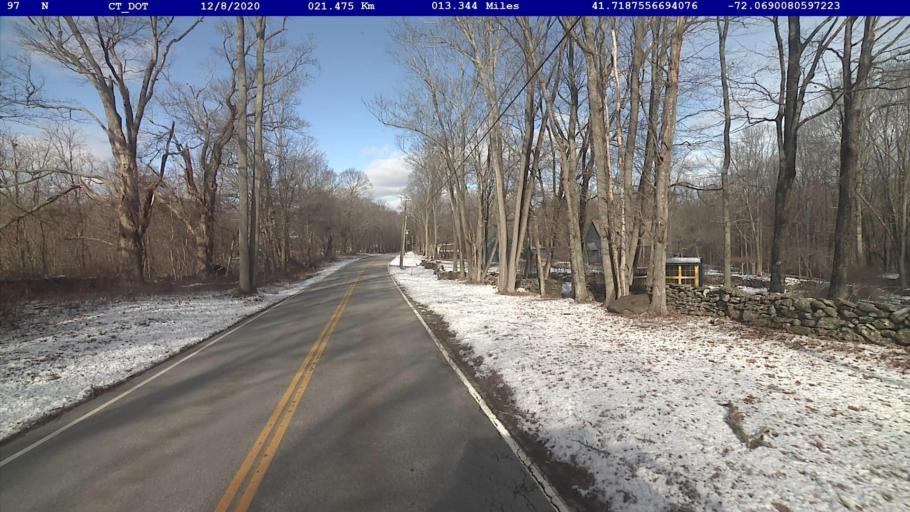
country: US
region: Connecticut
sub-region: Windham County
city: Windham
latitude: 41.7188
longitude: -72.0690
